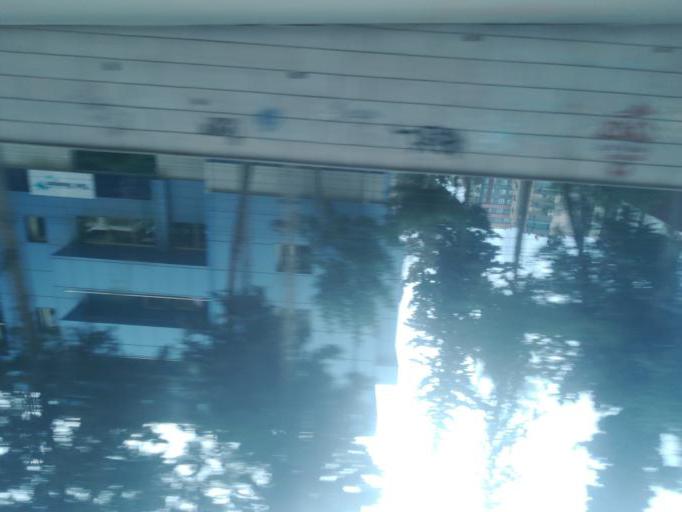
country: TR
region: Adana
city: Adana
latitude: 37.0407
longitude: 35.2923
